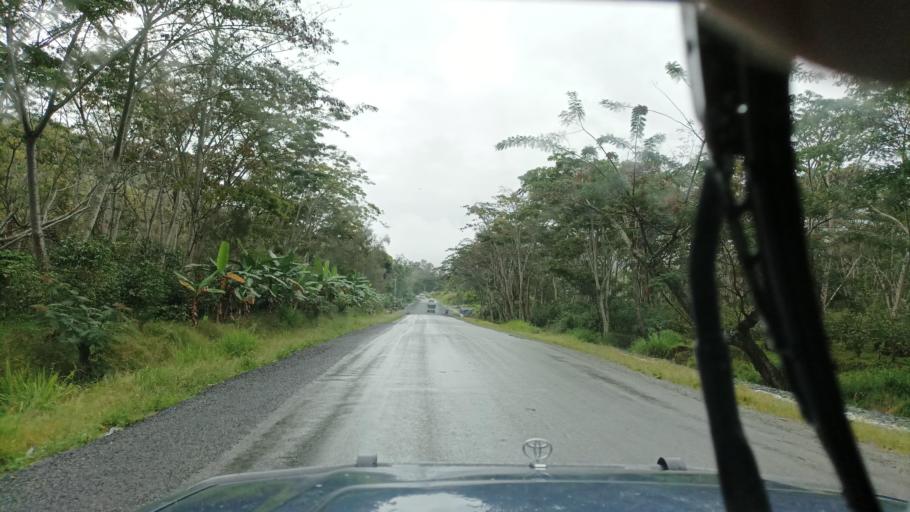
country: PG
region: Western Highlands
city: Rauna
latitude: -5.8332
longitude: 144.3521
